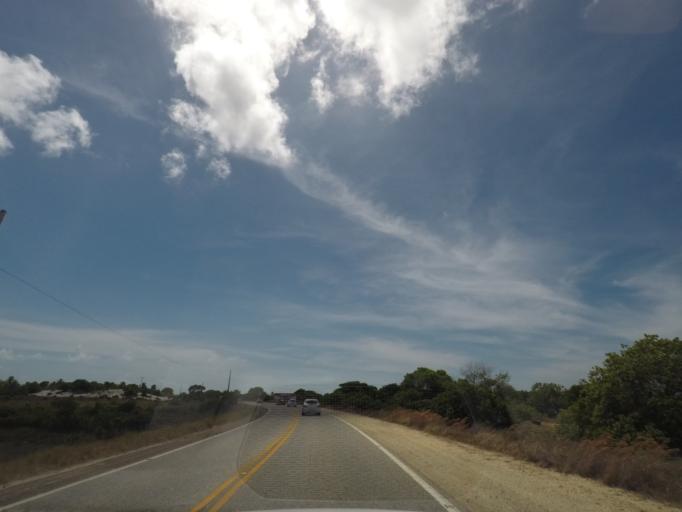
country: BR
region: Sergipe
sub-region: Sao Cristovao
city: Sao Cristovao
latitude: -11.1967
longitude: -37.2208
